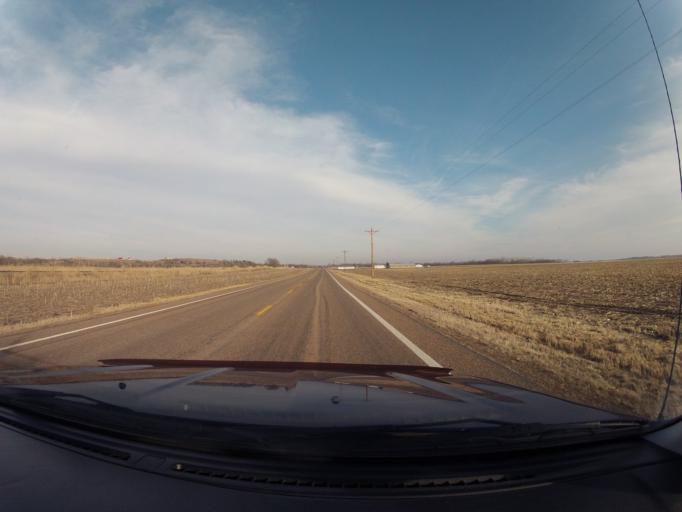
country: US
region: Kansas
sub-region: Pottawatomie County
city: Saint Marys
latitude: 39.2167
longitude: -96.1424
